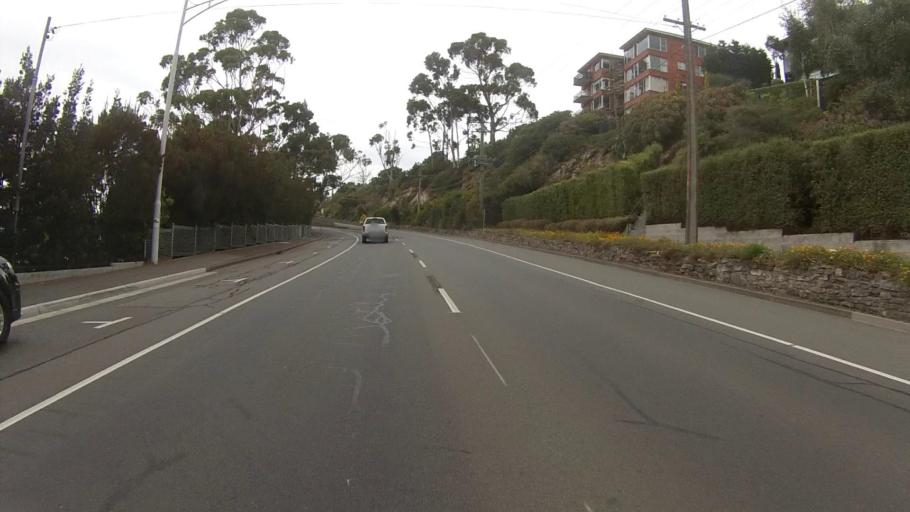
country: AU
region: Tasmania
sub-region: Kingborough
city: Taroona
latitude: -42.9138
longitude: 147.3566
